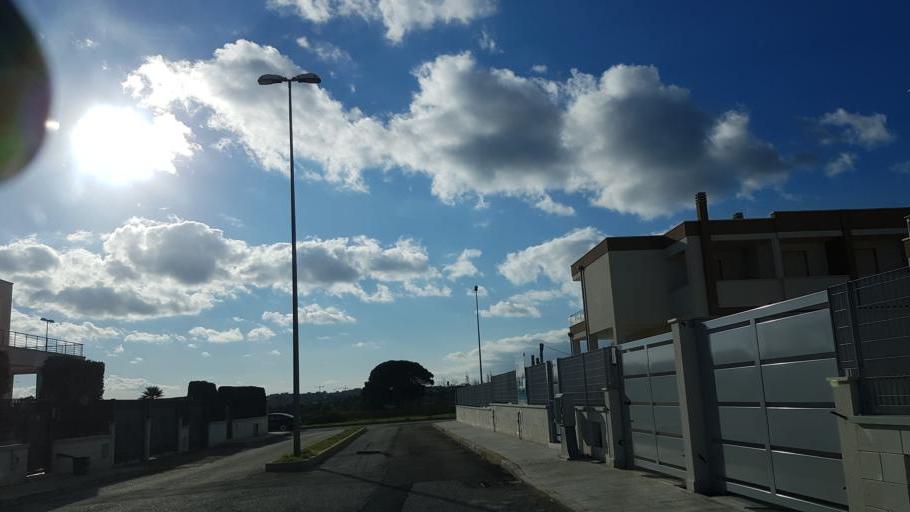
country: IT
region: Apulia
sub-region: Provincia di Brindisi
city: Brindisi
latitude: 40.6420
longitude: 17.9173
